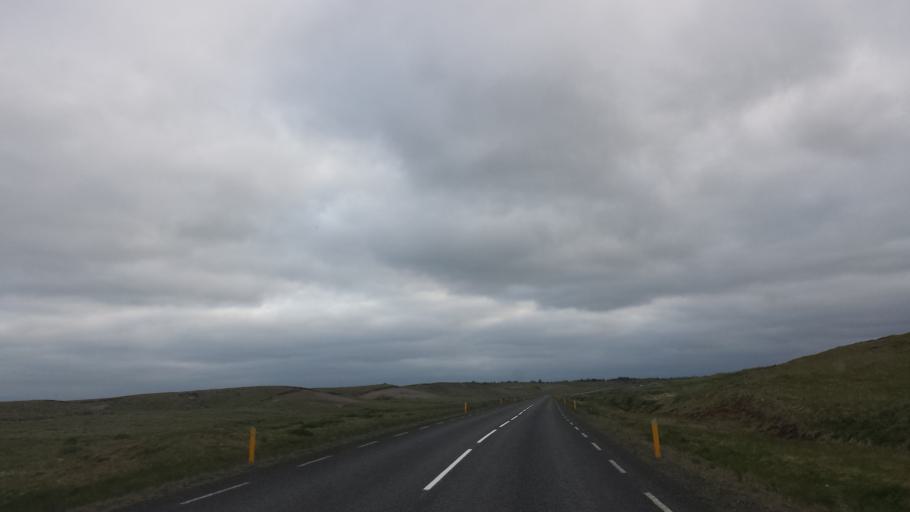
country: IS
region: South
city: Selfoss
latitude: 64.1293
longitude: -20.5856
